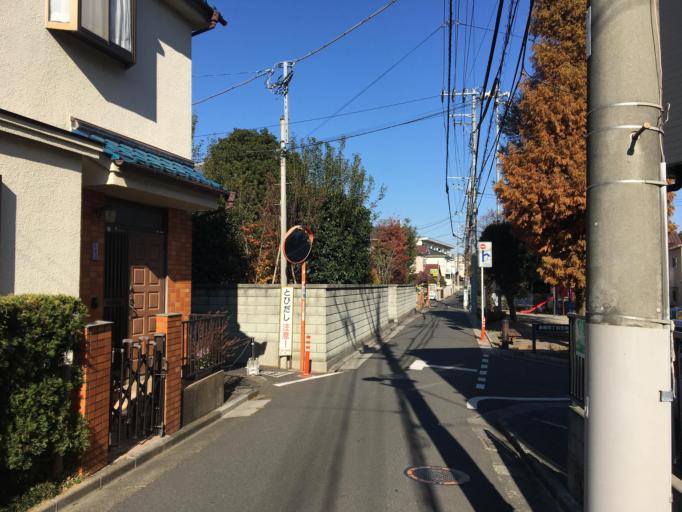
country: JP
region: Saitama
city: Wako
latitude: 35.7858
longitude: 139.6394
